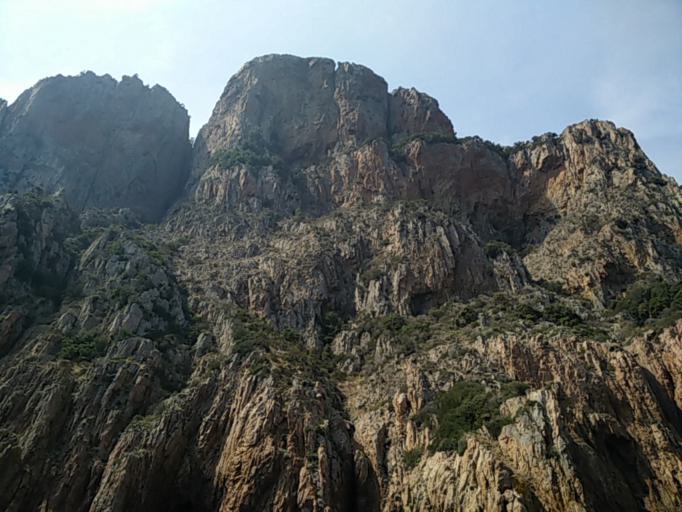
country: FR
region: Corsica
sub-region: Departement de la Corse-du-Sud
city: Cargese
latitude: 42.2388
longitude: 8.5535
